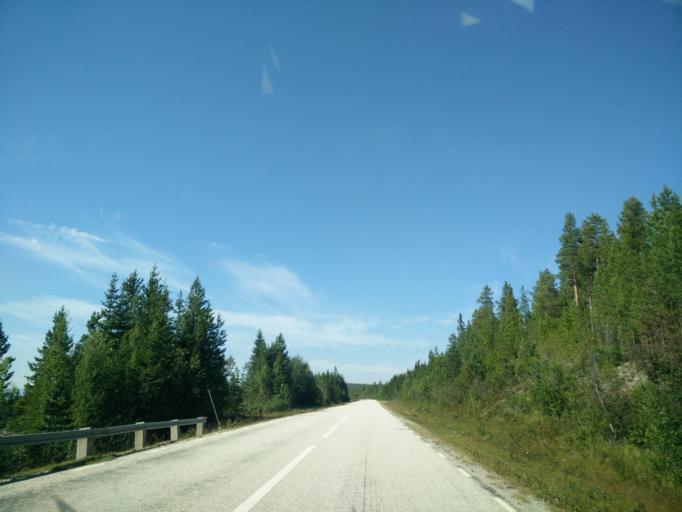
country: SE
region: Jaemtland
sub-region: Are Kommun
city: Jarpen
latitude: 62.8118
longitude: 13.5232
